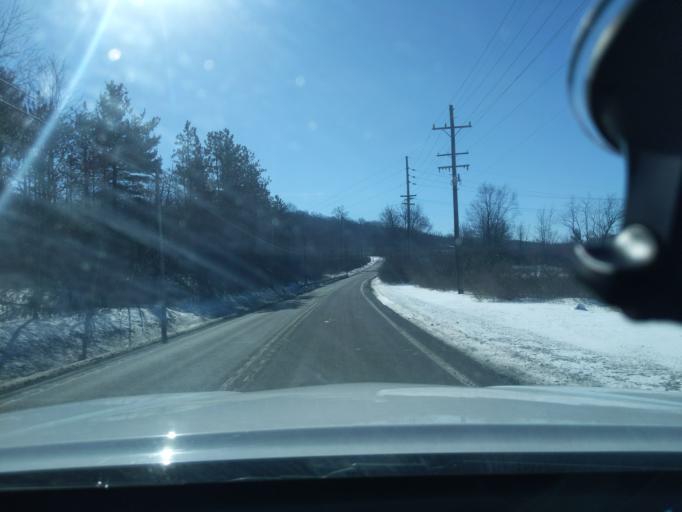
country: US
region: Maryland
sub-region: Allegany County
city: Frostburg
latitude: 39.6189
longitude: -78.9379
